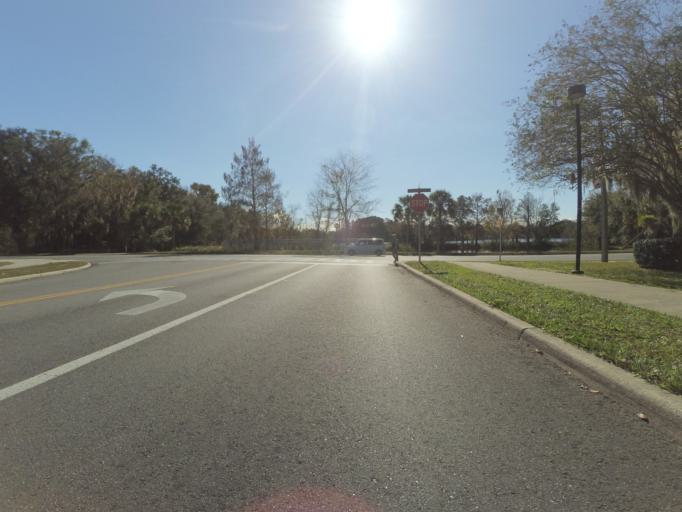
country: US
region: Florida
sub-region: Alachua County
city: Gainesville
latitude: 29.6455
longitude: -82.3600
